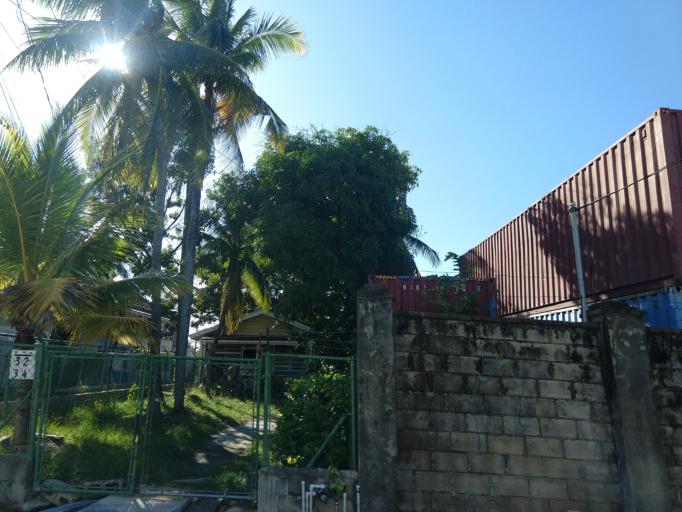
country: BZ
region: Belize
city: Belize City
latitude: 17.4988
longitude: -88.1843
